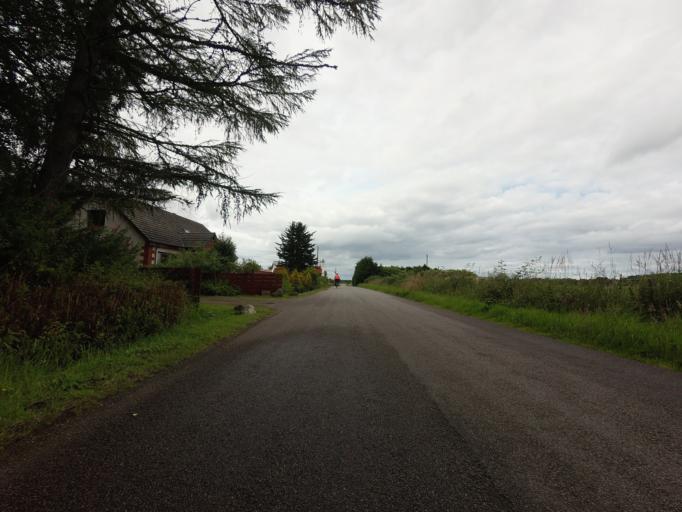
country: GB
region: Scotland
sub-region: Moray
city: Forres
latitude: 57.6032
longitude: -3.7261
